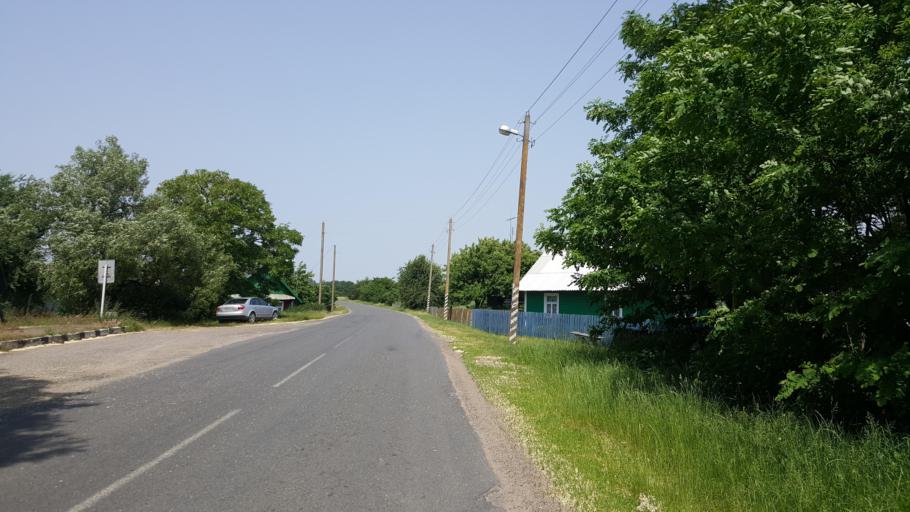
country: BY
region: Brest
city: Kamyanyuki
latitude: 52.4820
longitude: 23.8772
